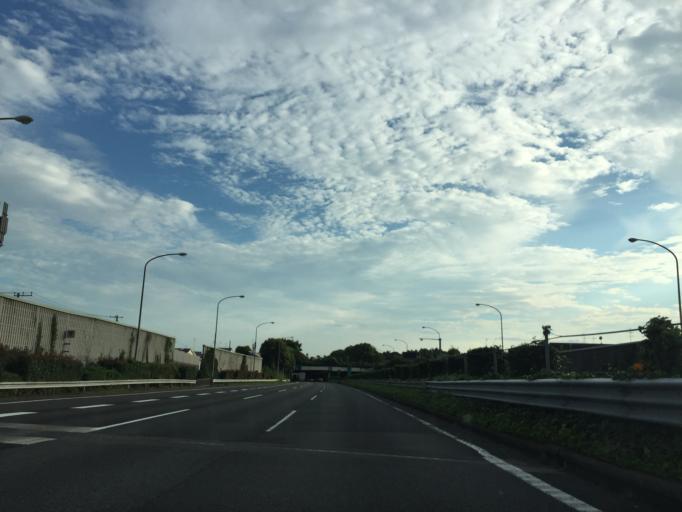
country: JP
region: Kanagawa
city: Minami-rinkan
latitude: 35.4789
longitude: 139.4535
